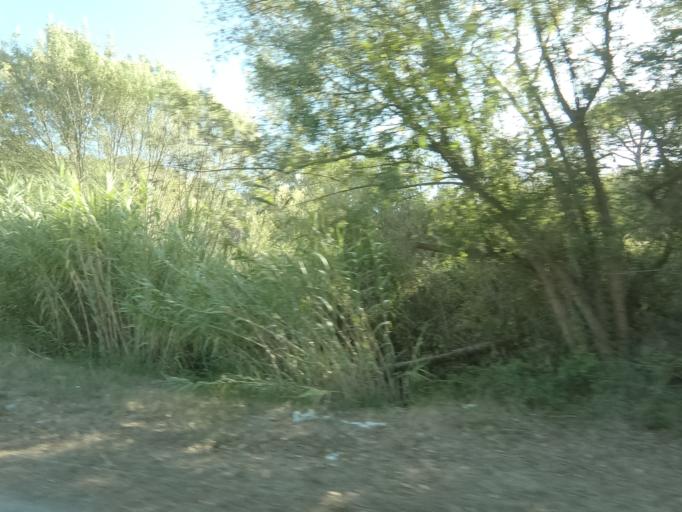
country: PT
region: Setubal
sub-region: Palmela
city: Quinta do Anjo
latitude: 38.5066
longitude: -8.9722
